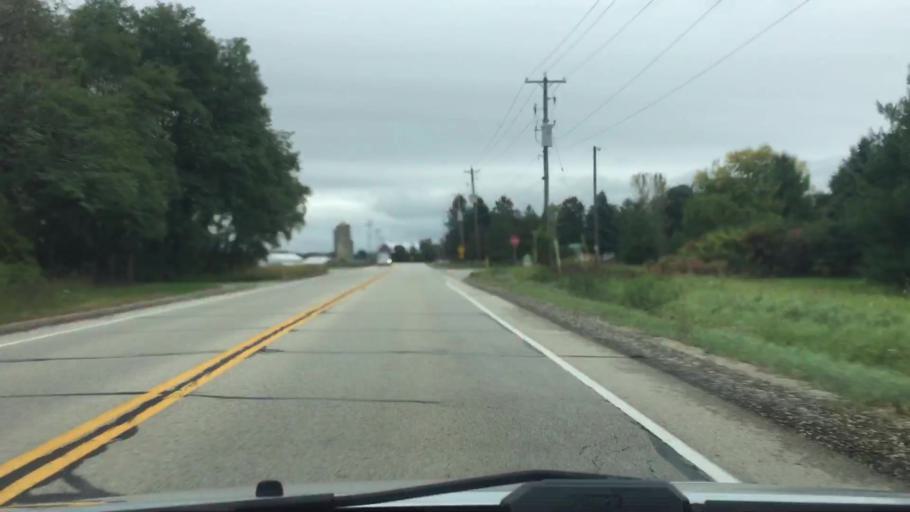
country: US
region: Wisconsin
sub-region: Jefferson County
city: Palmyra
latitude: 42.7825
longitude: -88.5573
